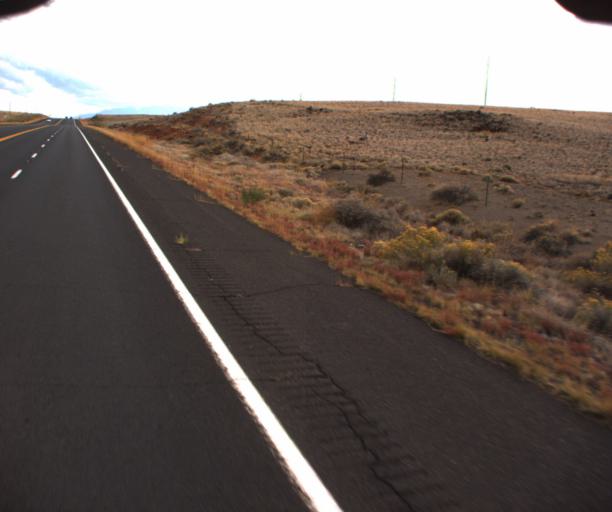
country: US
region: Arizona
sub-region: Coconino County
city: Flagstaff
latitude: 35.6571
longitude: -111.5142
